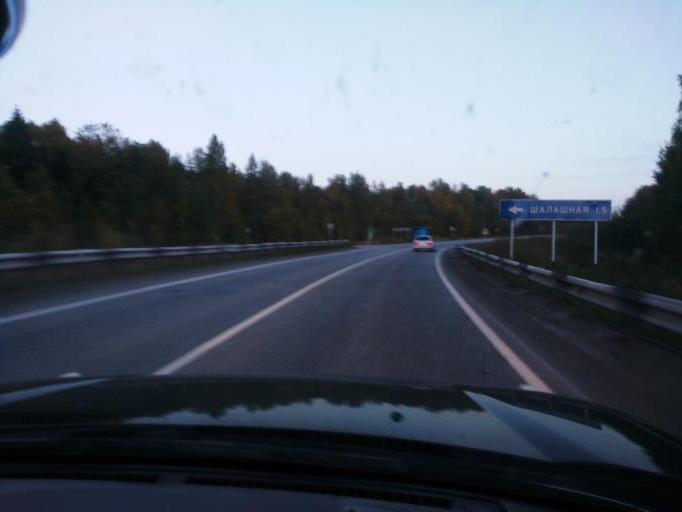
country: RU
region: Perm
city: Verkhnechusovskiye Gorodki
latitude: 58.2916
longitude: 56.8957
